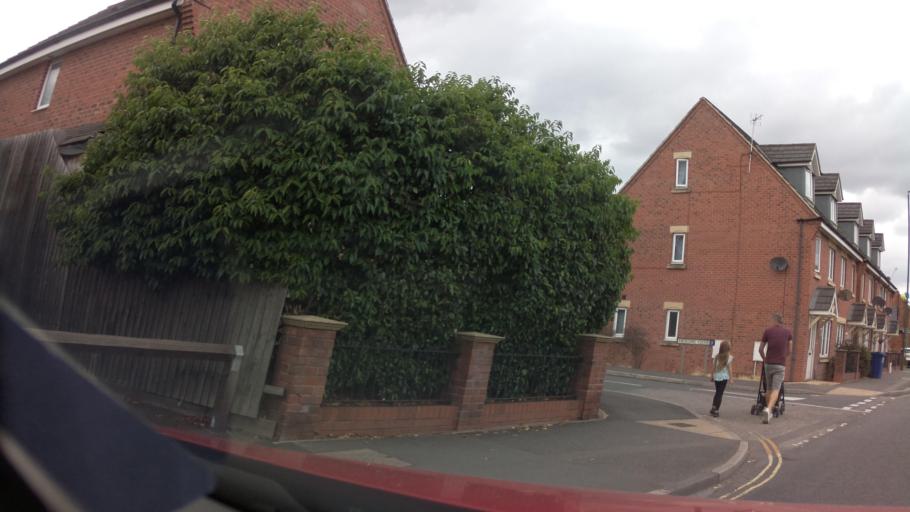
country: GB
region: England
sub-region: Derbyshire
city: Long Eaton
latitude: 52.8869
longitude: -1.2872
